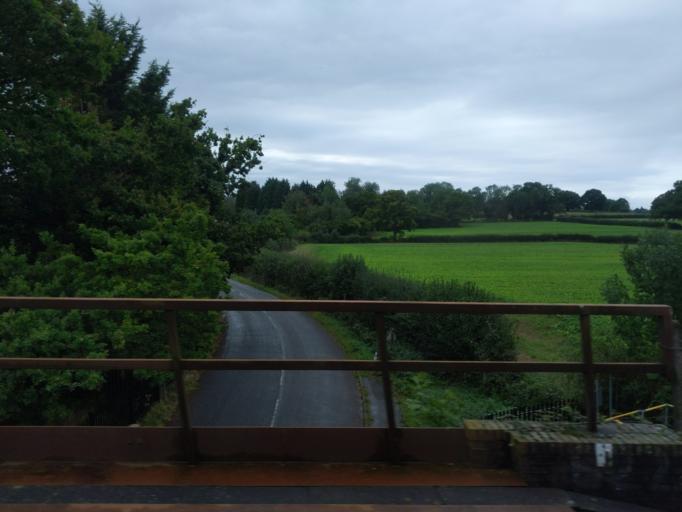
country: GB
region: England
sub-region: Kent
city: Tonbridge
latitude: 51.2085
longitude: 0.2439
